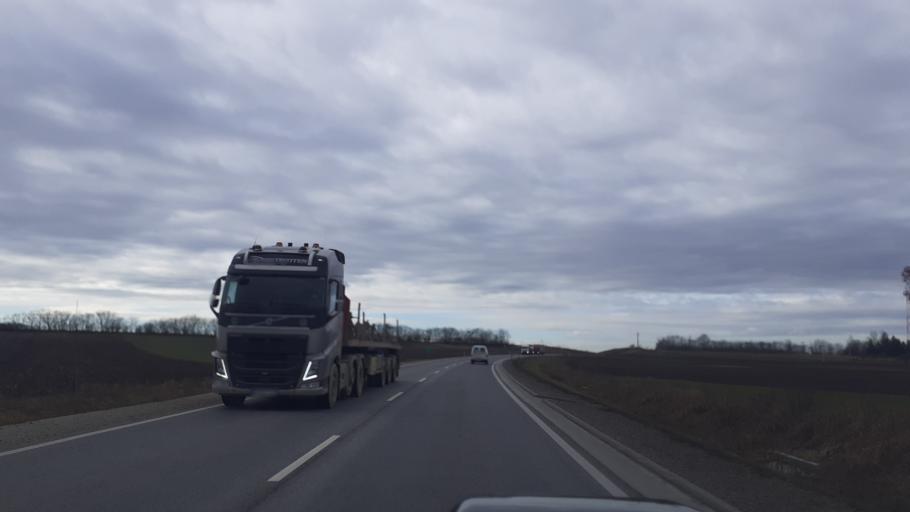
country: HU
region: Fejer
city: Seregelyes
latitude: 47.0937
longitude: 18.5875
